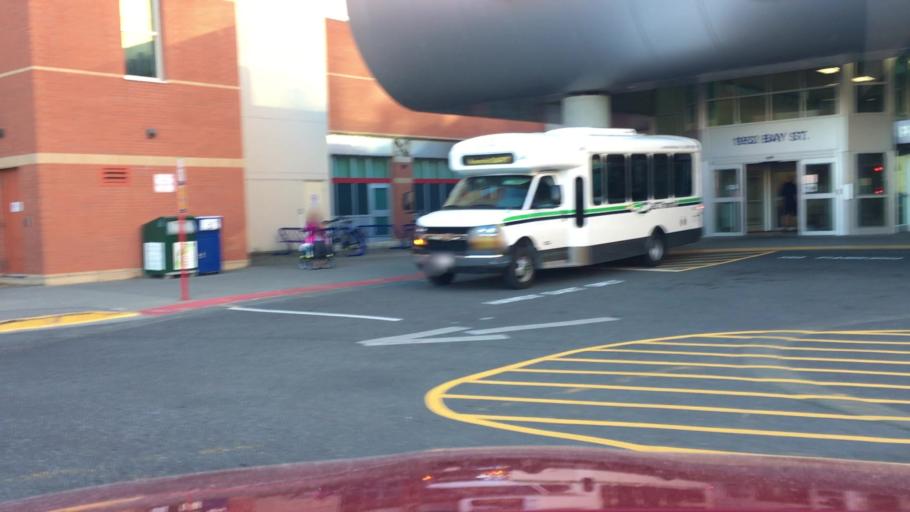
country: CA
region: British Columbia
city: Oak Bay
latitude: 48.4335
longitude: -123.3274
